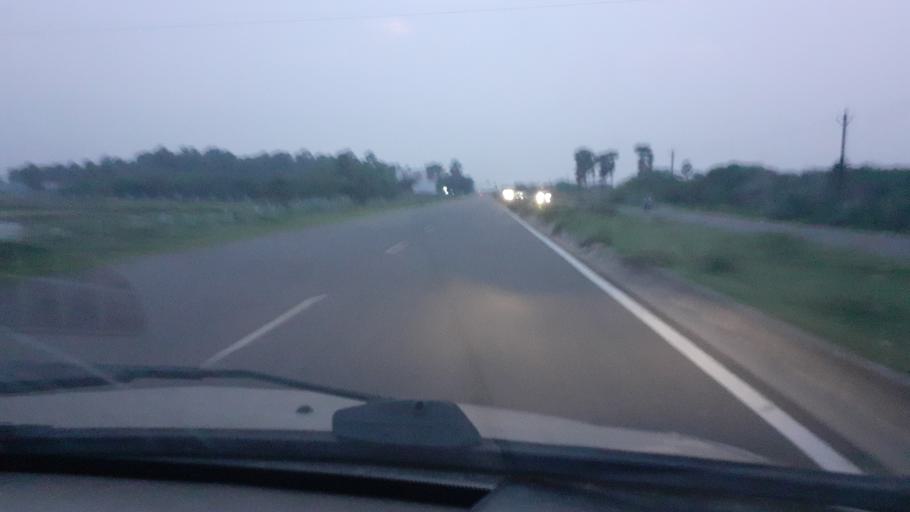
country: IN
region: Tamil Nadu
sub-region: Thoothukkudi
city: Srivaikuntam
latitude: 8.7075
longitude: 77.8168
